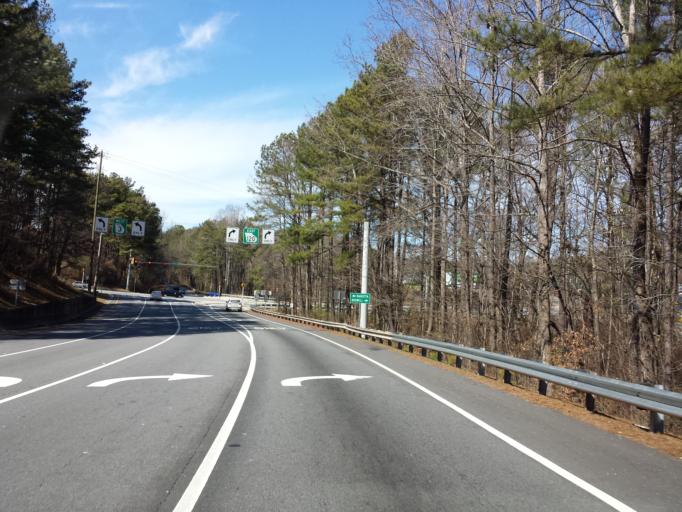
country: US
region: Georgia
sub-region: Cobb County
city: Marietta
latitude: 33.9598
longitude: -84.4960
